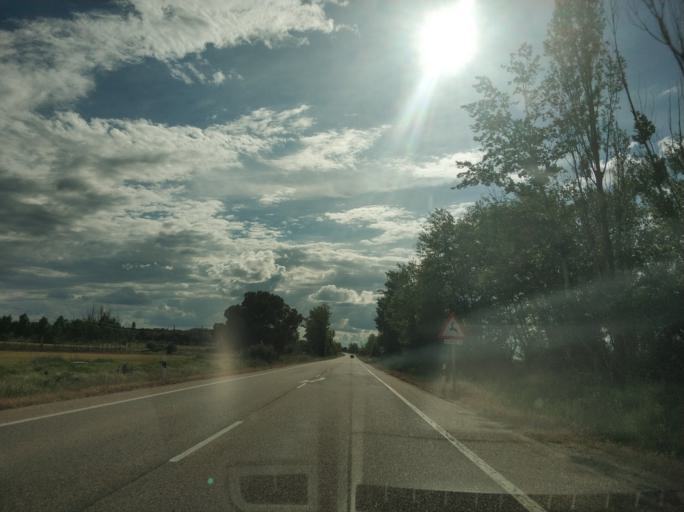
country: ES
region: Castille and Leon
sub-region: Provincia de Burgos
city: Villalba de Duero
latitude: 41.6620
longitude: -3.7489
